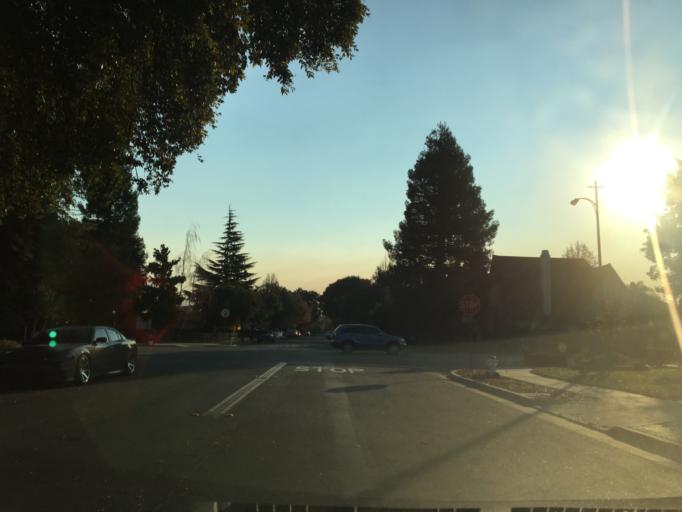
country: US
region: California
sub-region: Santa Clara County
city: Sunnyvale
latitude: 37.3917
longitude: -122.0251
